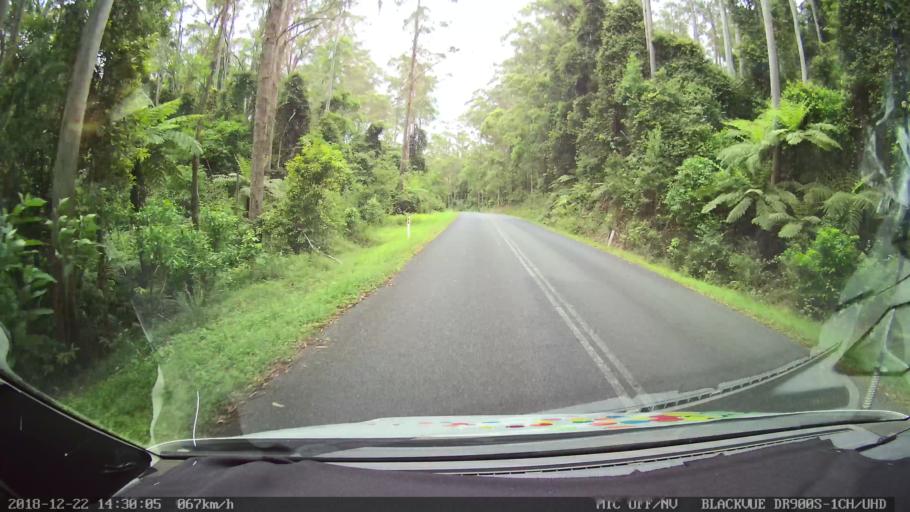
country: AU
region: New South Wales
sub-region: Bellingen
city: Dorrigo
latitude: -30.0824
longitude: 152.6331
